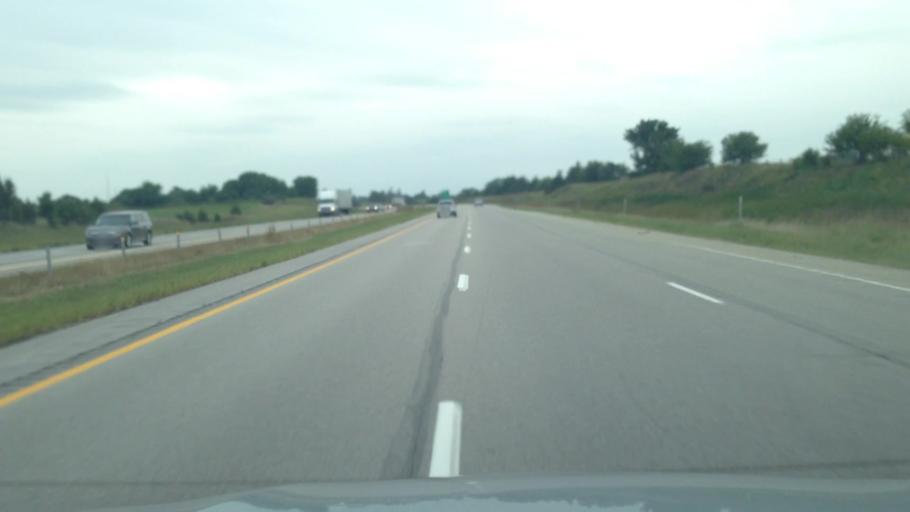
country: US
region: Iowa
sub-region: Clarke County
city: Osceola
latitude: 41.0400
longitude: -93.7924
